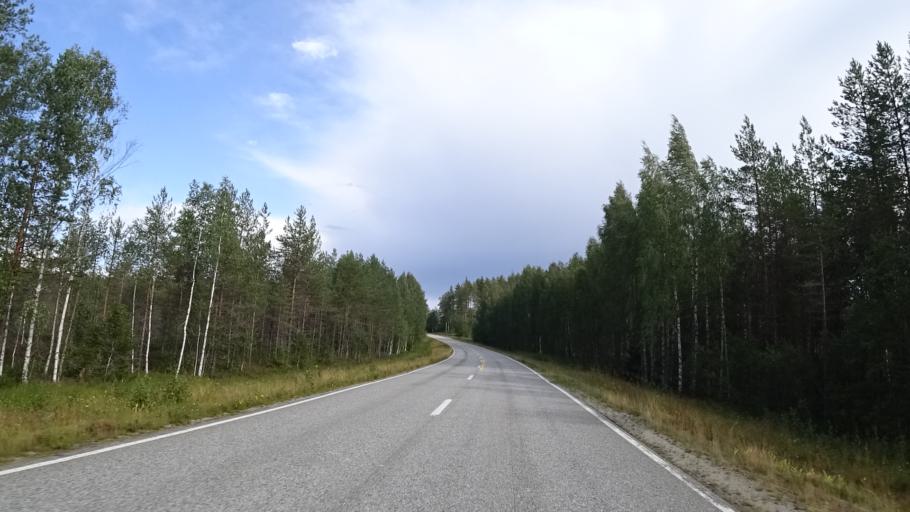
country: FI
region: North Karelia
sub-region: Joensuu
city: Ilomantsi
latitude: 62.6212
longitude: 31.1666
